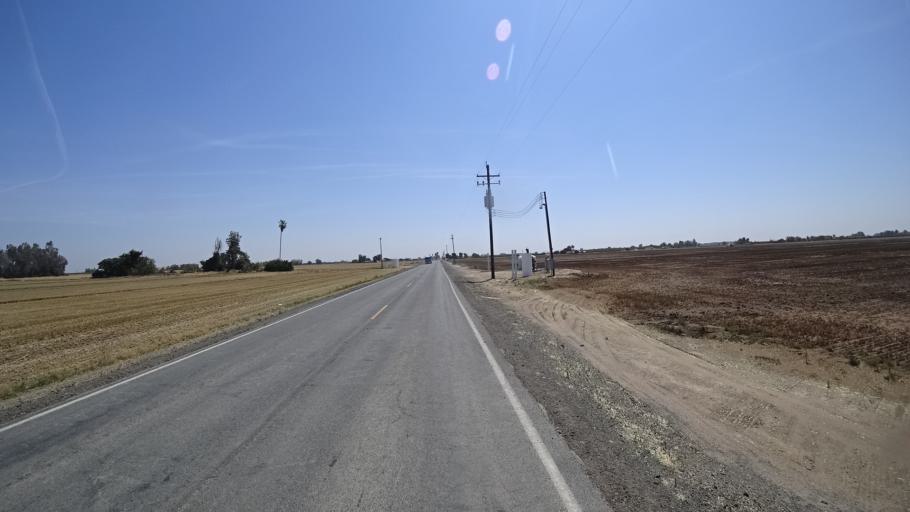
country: US
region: California
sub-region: Fresno County
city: Riverdale
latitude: 36.4022
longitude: -119.8417
